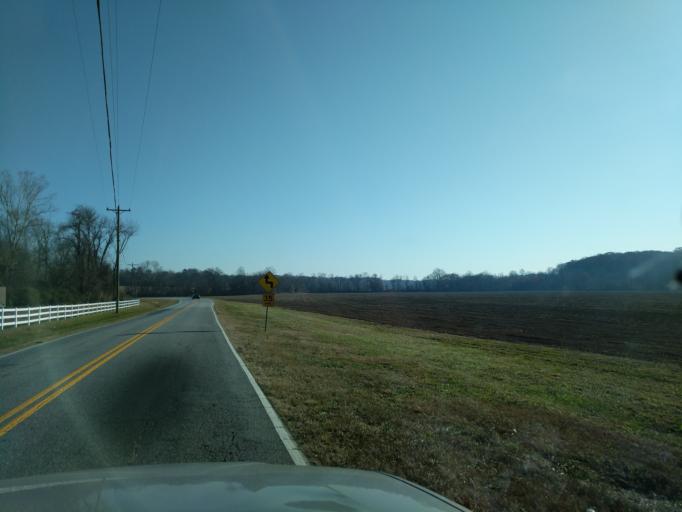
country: US
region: South Carolina
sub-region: Spartanburg County
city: Landrum
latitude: 35.1868
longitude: -82.1482
